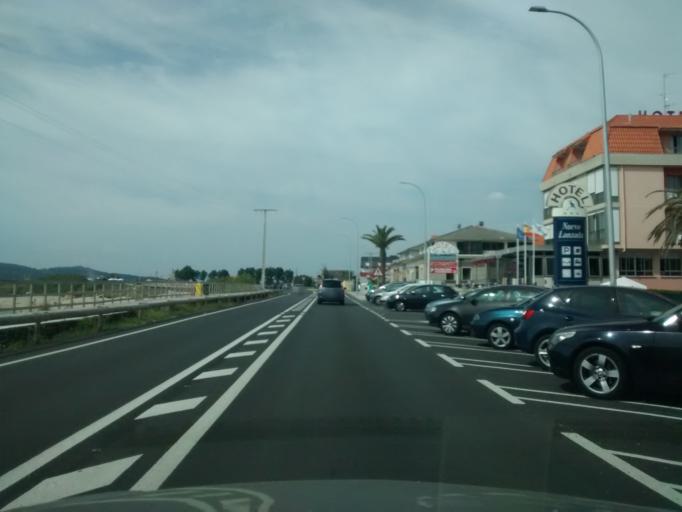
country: ES
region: Galicia
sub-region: Provincia de Pontevedra
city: O Grove
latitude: 42.4333
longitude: -8.8710
